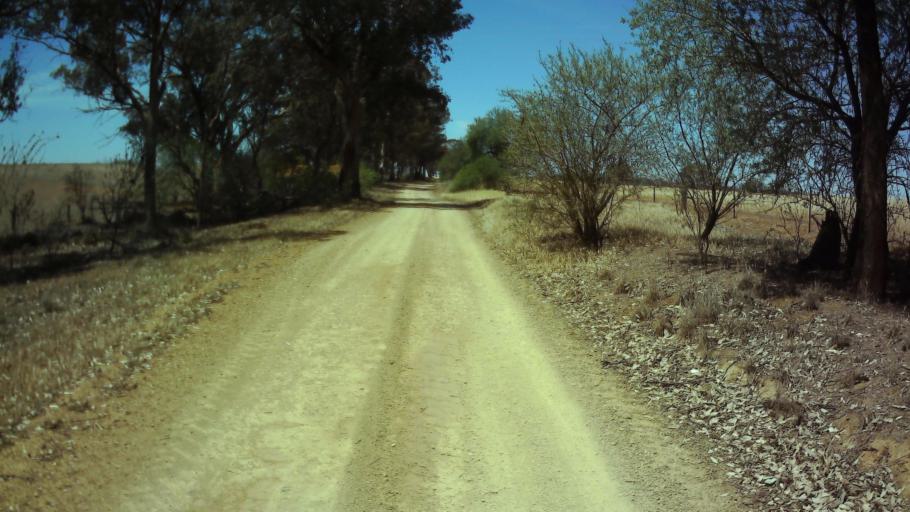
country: AU
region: New South Wales
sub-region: Weddin
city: Grenfell
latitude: -33.9284
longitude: 148.1747
